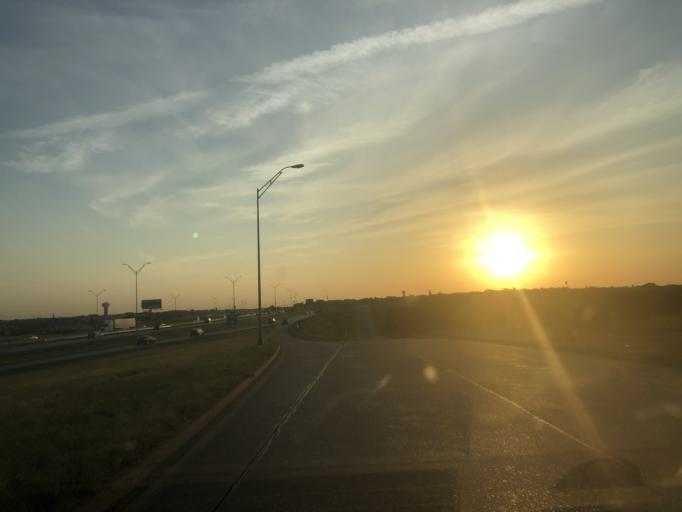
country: US
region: Texas
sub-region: Tarrant County
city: Lake Worth
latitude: 32.8032
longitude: -97.4249
